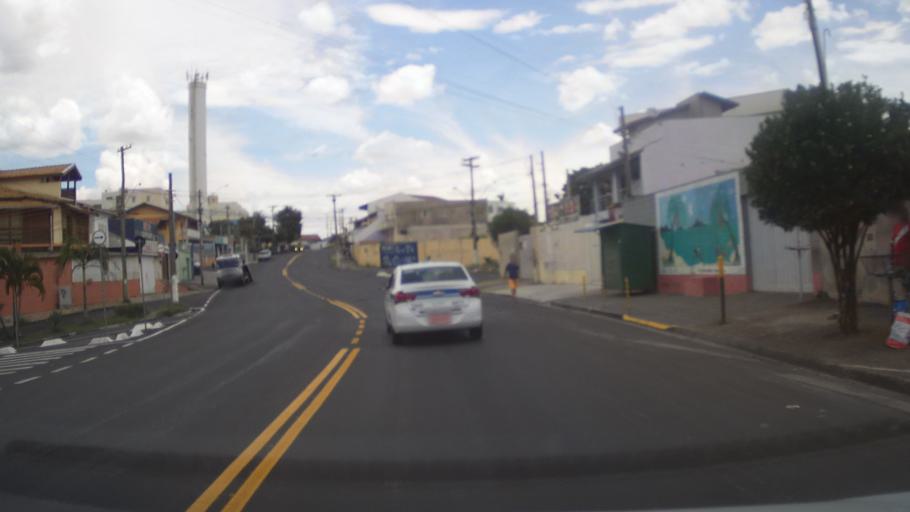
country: BR
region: Sao Paulo
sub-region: Campinas
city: Campinas
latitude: -22.9186
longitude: -47.0183
